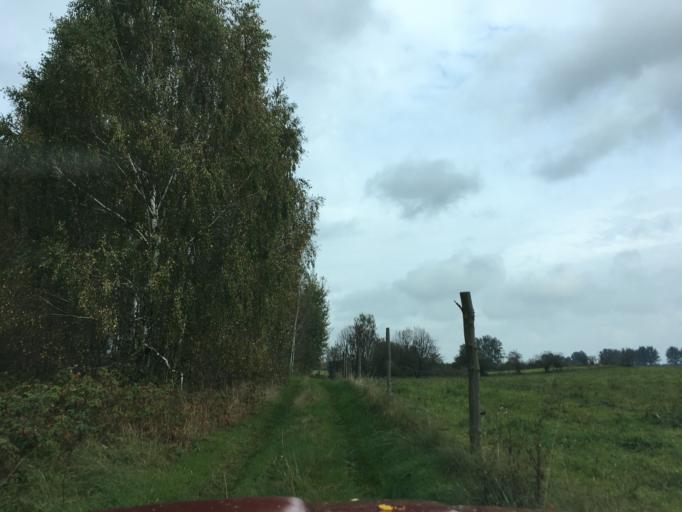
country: PL
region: Warmian-Masurian Voivodeship
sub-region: Powiat dzialdowski
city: Rybno
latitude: 53.4148
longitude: 19.9127
